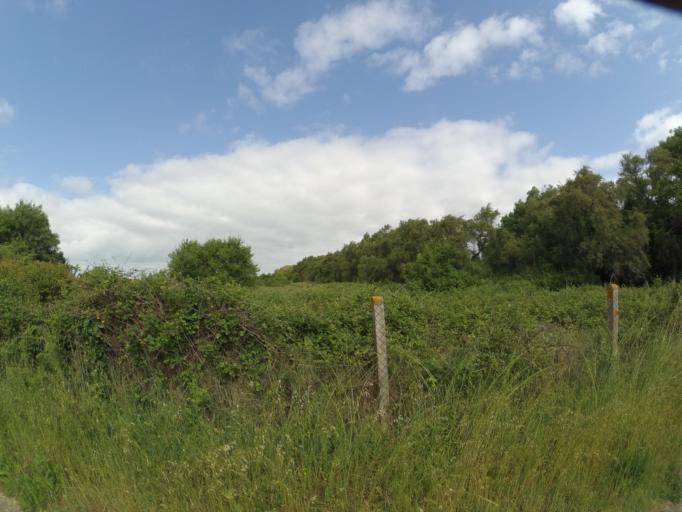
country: FR
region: Poitou-Charentes
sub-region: Departement de la Charente-Maritime
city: Angoulins
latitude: 46.1061
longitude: -1.1166
